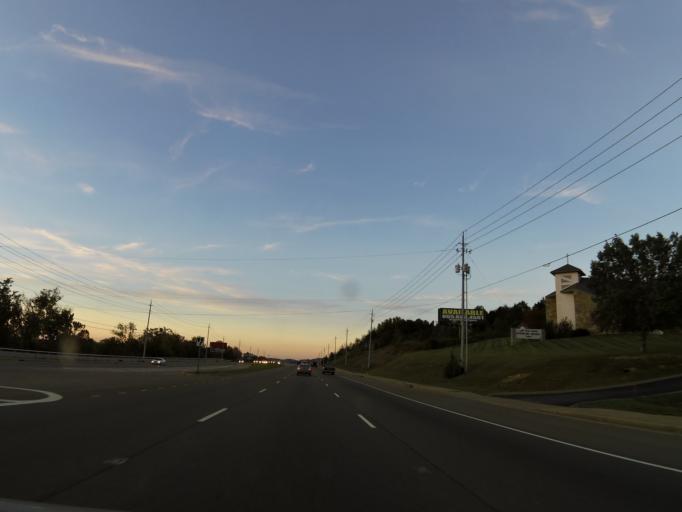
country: US
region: Tennessee
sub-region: Sevier County
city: Sevierville
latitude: 35.8966
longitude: -83.5809
